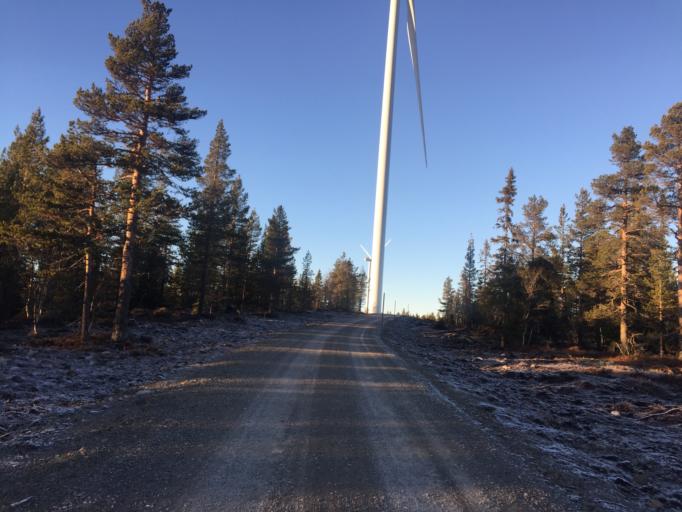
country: NO
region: Hedmark
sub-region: Elverum
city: Elverum
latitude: 61.2069
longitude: 11.7888
